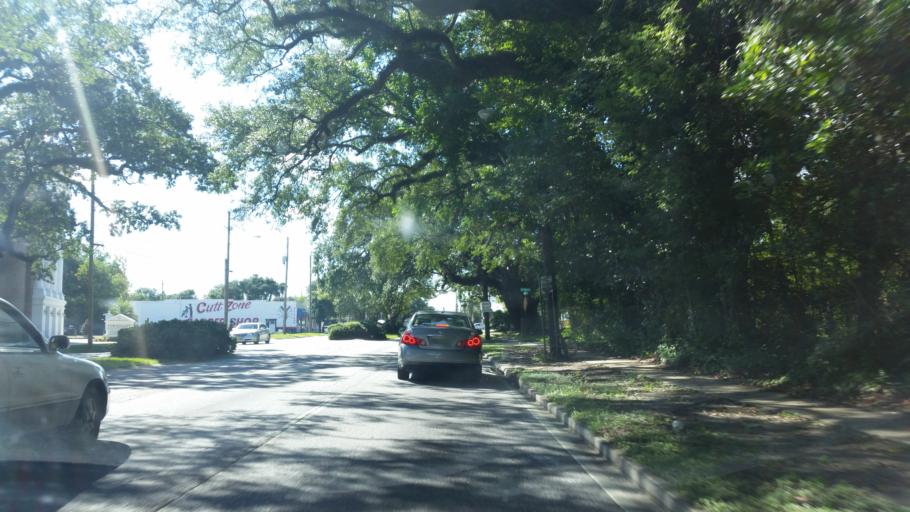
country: US
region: Alabama
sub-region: Mobile County
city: Prichard
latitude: 30.6962
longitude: -88.1020
